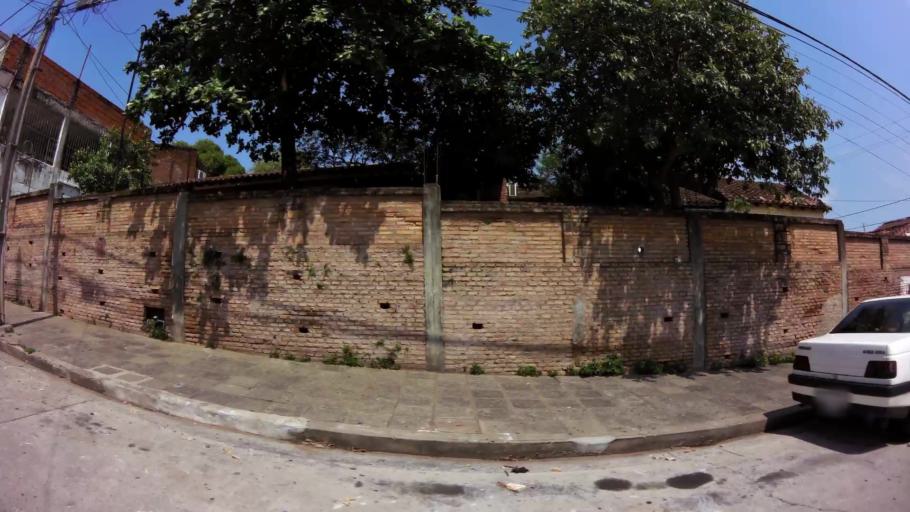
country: PY
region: Presidente Hayes
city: Nanawa
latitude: -25.2774
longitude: -57.6546
